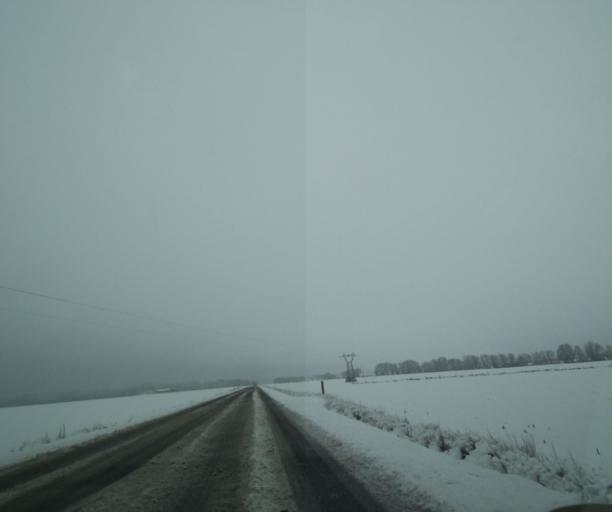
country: FR
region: Champagne-Ardenne
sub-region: Departement de la Haute-Marne
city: Saint-Dizier
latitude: 48.5766
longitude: 4.9088
